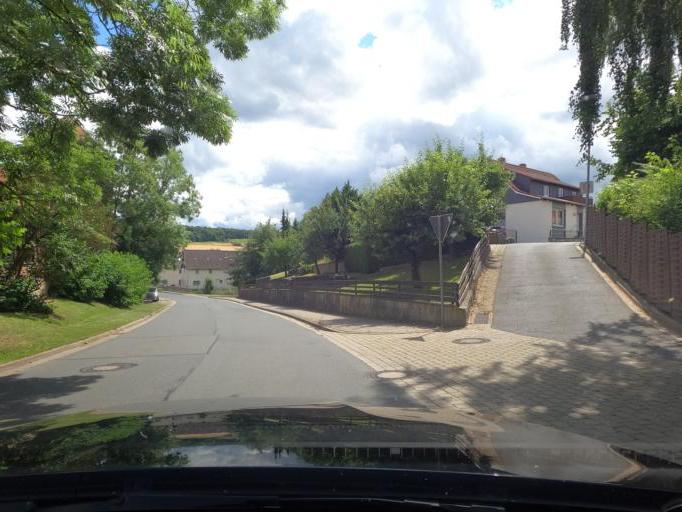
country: DE
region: Lower Saxony
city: Baddeckenstedt
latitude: 52.1017
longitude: 10.2356
